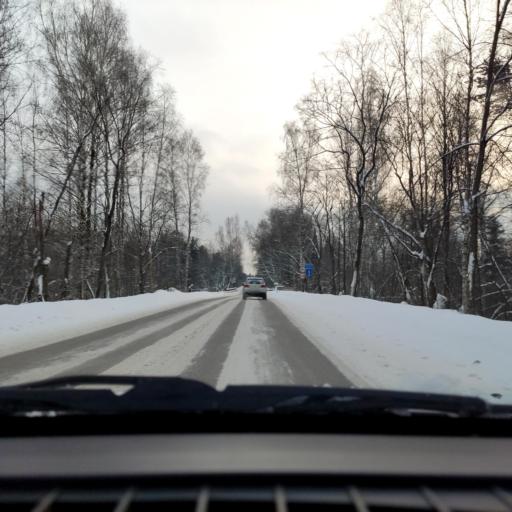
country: RU
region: Perm
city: Overyata
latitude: 58.0517
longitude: 55.8843
